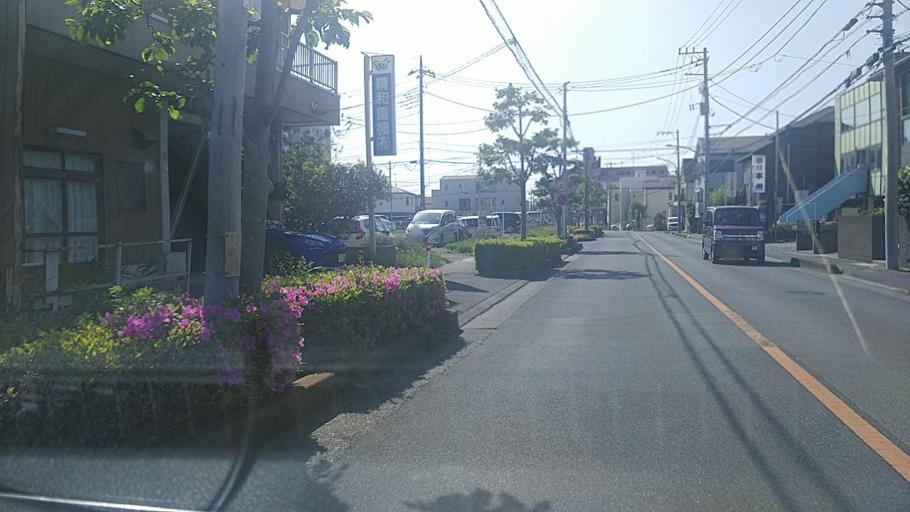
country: JP
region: Saitama
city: Koshigaya
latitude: 35.8810
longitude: 139.7476
